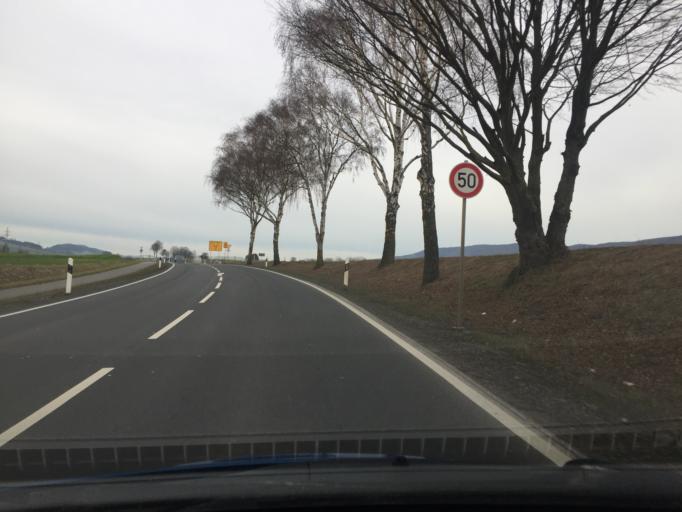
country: DE
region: Lower Saxony
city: Luerdissen
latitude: 51.9417
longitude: 9.6314
